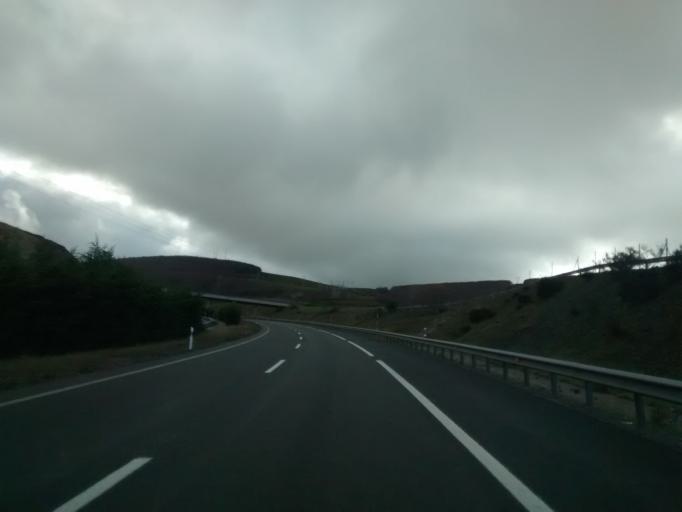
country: ES
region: Cantabria
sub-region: Provincia de Cantabria
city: Villaescusa
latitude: 42.9583
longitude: -4.1564
